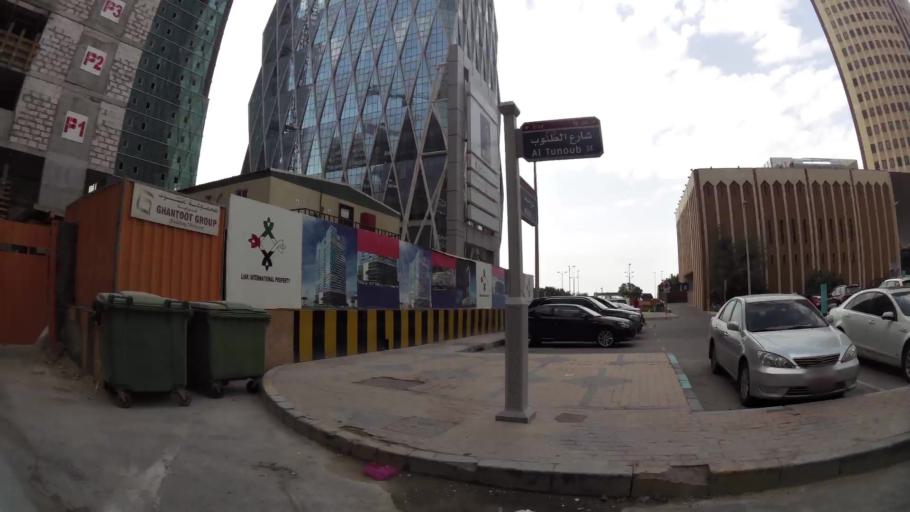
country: AE
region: Abu Dhabi
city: Abu Dhabi
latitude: 24.4878
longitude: 54.3528
